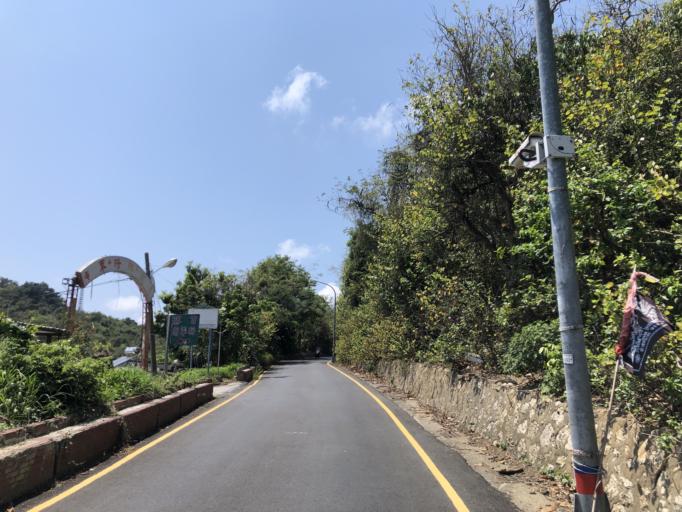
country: TW
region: Kaohsiung
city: Kaohsiung
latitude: 22.6259
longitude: 120.2719
